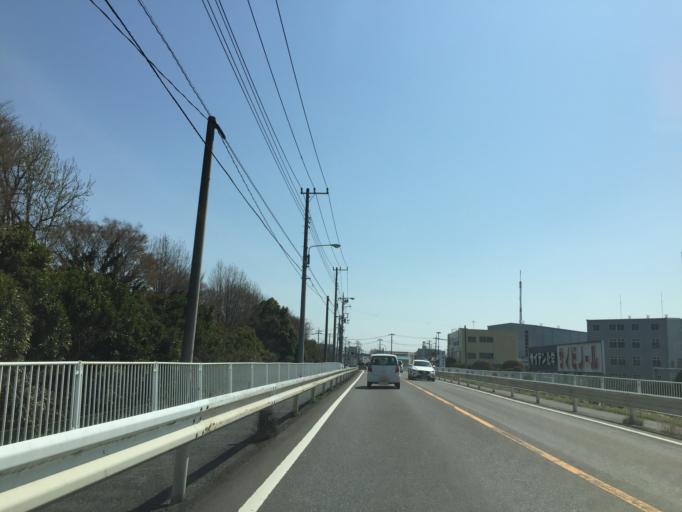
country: JP
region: Saitama
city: Shiki
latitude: 35.8591
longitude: 139.6069
